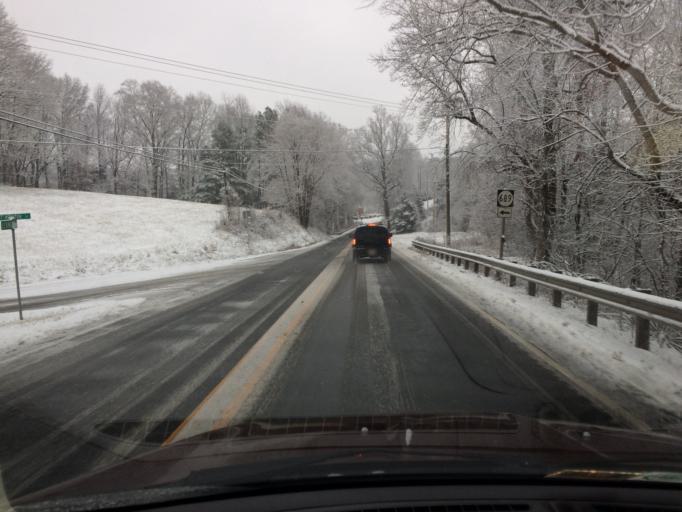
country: US
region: Virginia
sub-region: Amherst County
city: Amherst
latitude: 37.5967
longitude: -79.0562
